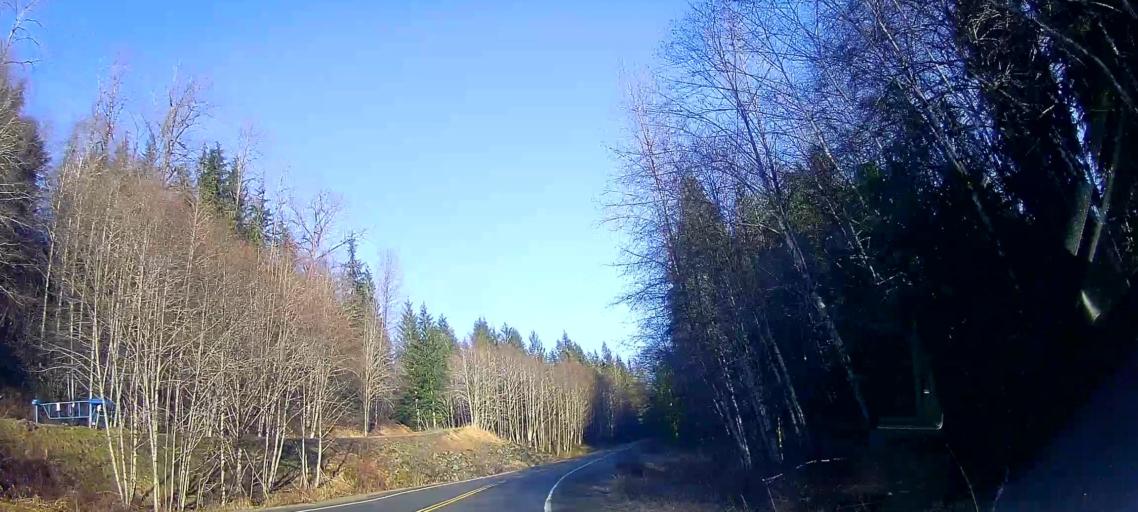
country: US
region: Washington
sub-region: Snohomish County
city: Darrington
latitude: 48.6213
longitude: -121.7474
